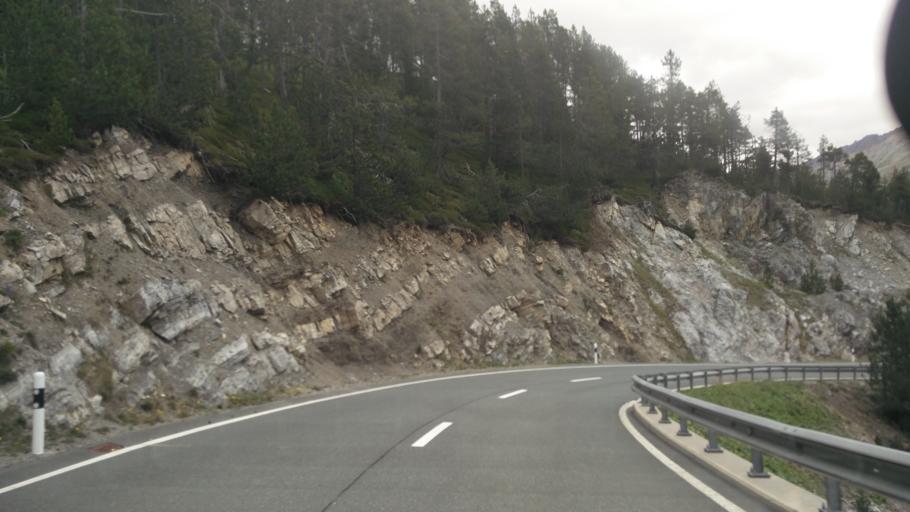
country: IT
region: Lombardy
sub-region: Provincia di Sondrio
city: Isolaccia
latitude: 46.6380
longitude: 10.3013
